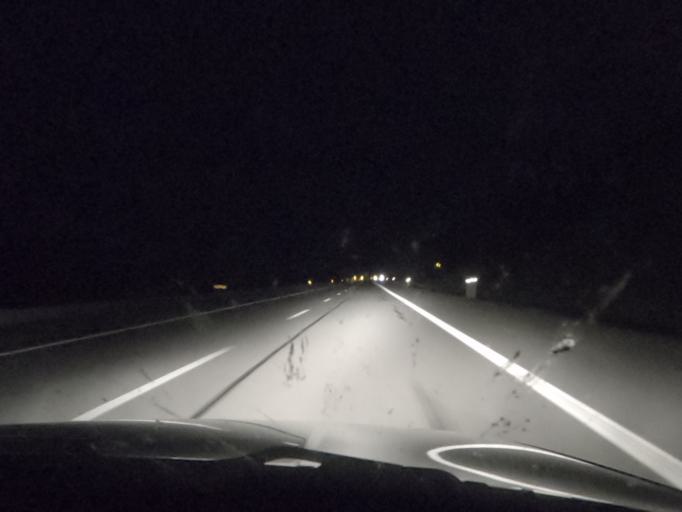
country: PT
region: Evora
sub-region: Estremoz
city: Estremoz
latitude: 38.8325
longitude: -7.6118
